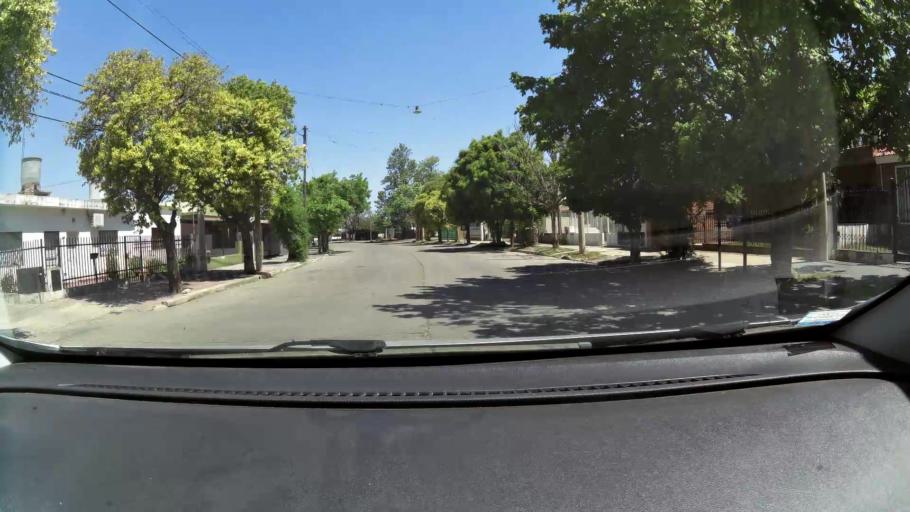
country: AR
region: Cordoba
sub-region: Departamento de Capital
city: Cordoba
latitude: -31.3818
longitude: -64.1657
